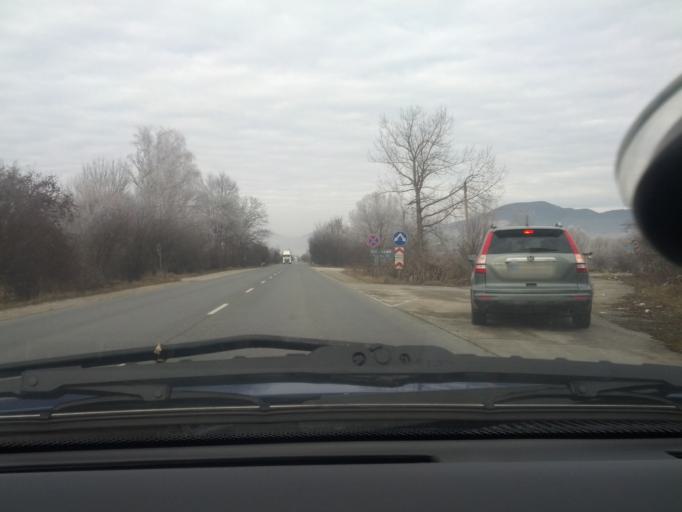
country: BG
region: Sofiya
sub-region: Obshtina Botevgrad
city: Botevgrad
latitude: 42.9332
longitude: 23.7756
